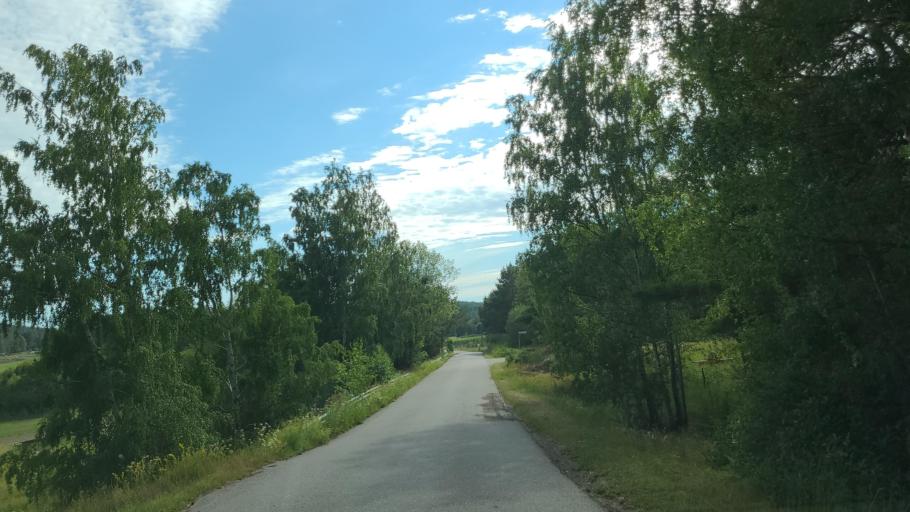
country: FI
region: Varsinais-Suomi
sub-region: Turku
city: Rymaettylae
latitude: 60.3005
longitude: 21.9416
